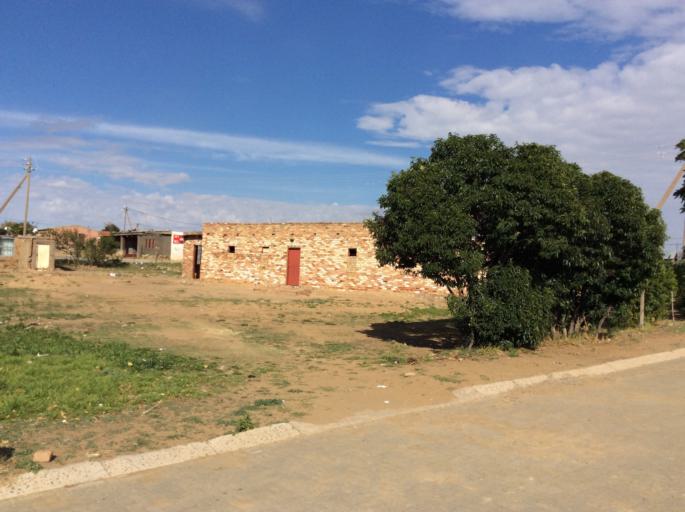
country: LS
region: Mafeteng
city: Mafeteng
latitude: -29.7184
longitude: 27.0127
